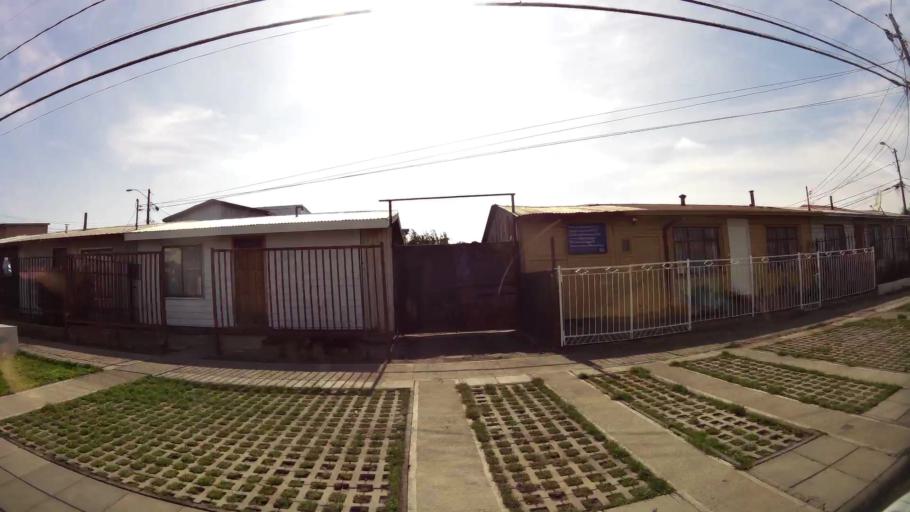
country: CL
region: Biobio
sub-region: Provincia de Concepcion
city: Talcahuano
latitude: -36.7843
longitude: -73.1145
